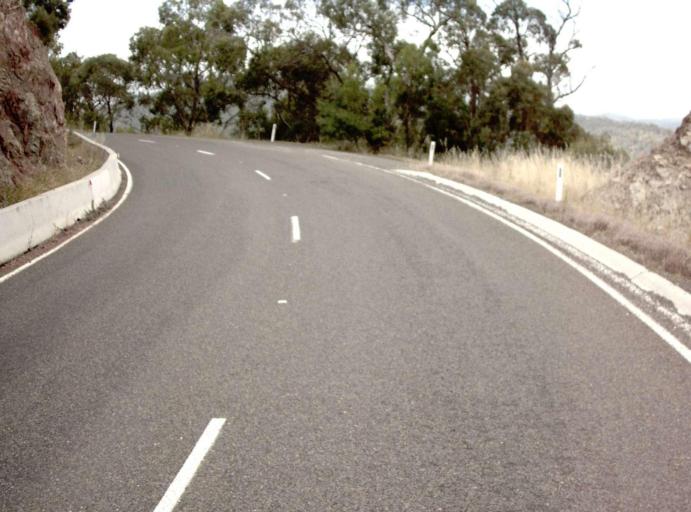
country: AU
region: Victoria
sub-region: Wellington
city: Heyfield
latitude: -37.7104
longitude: 146.6643
